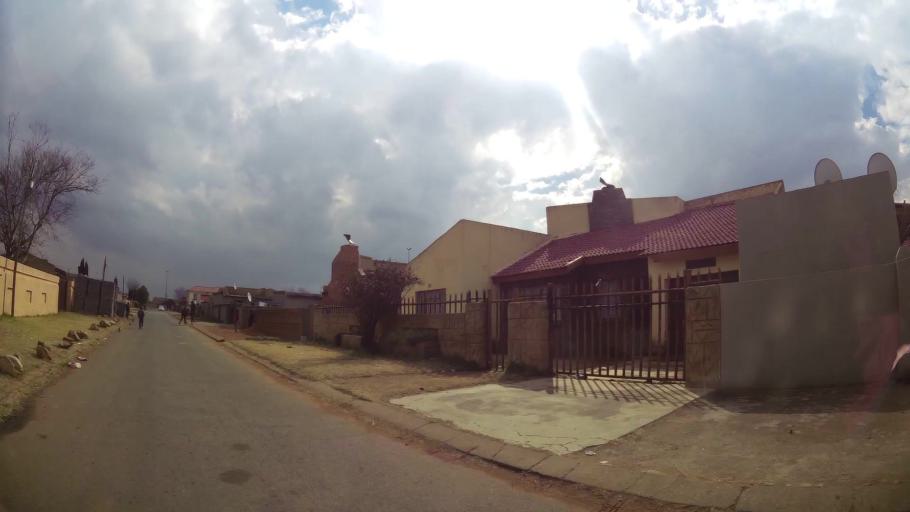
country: ZA
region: Gauteng
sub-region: Ekurhuleni Metropolitan Municipality
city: Germiston
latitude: -26.3880
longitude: 28.1567
